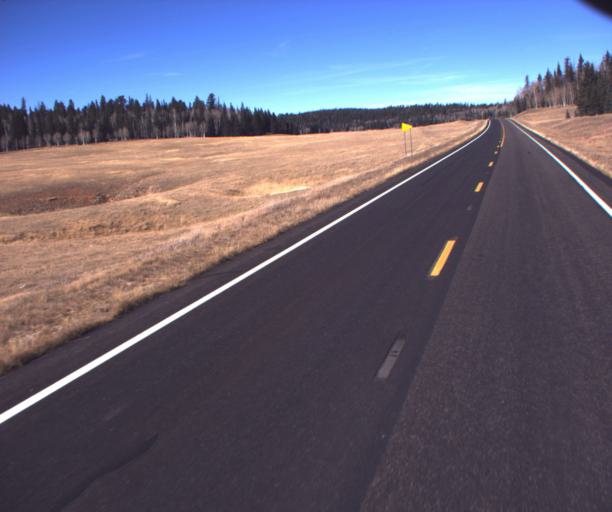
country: US
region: Arizona
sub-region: Coconino County
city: Grand Canyon
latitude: 36.4315
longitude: -112.1327
